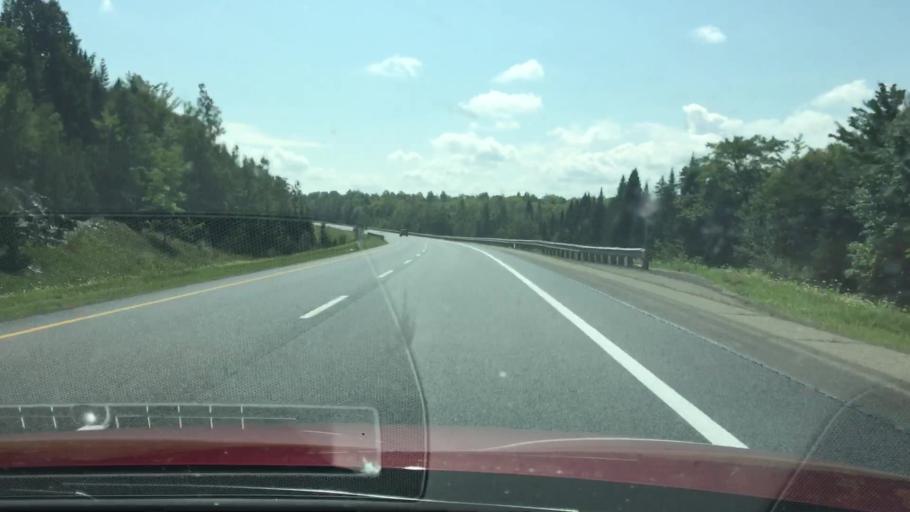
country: US
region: Maine
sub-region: Penobscot County
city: Patten
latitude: 45.8432
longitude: -68.4328
